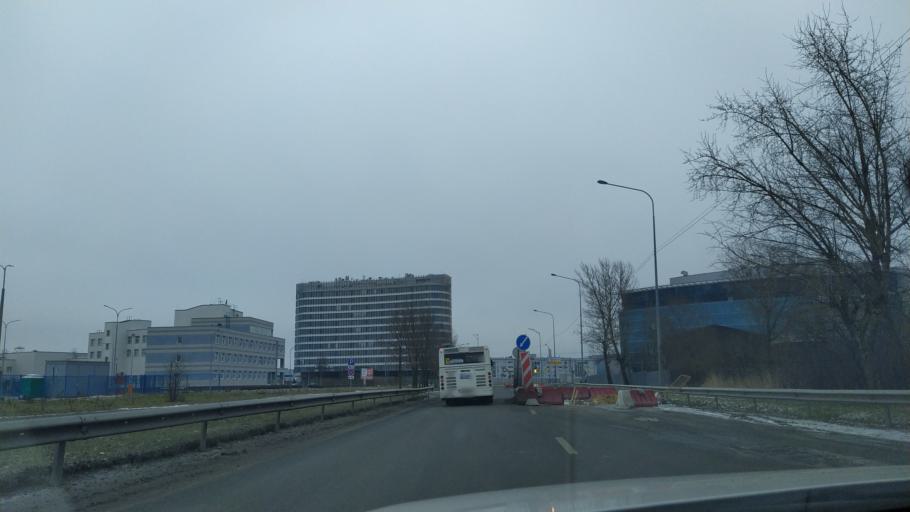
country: RU
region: St.-Petersburg
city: Kupchino
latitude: 59.8092
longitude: 30.3116
